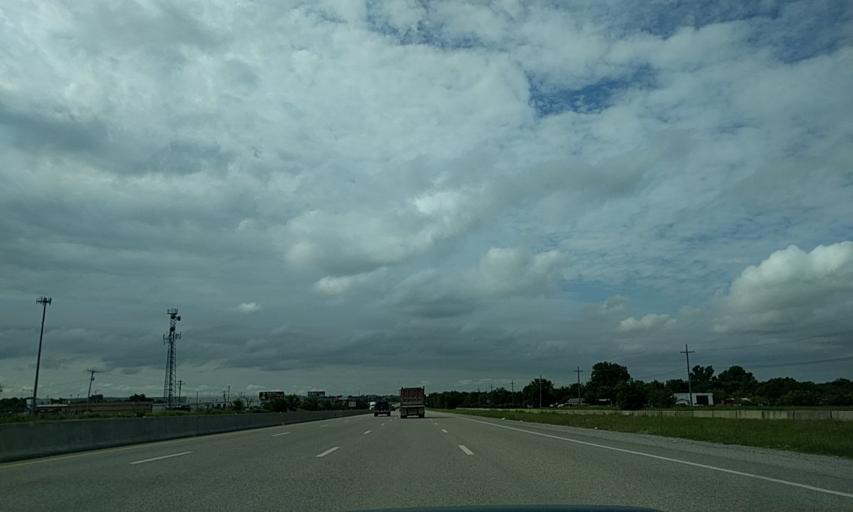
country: US
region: Oklahoma
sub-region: Tulsa County
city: Owasso
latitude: 36.2025
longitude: -95.8519
